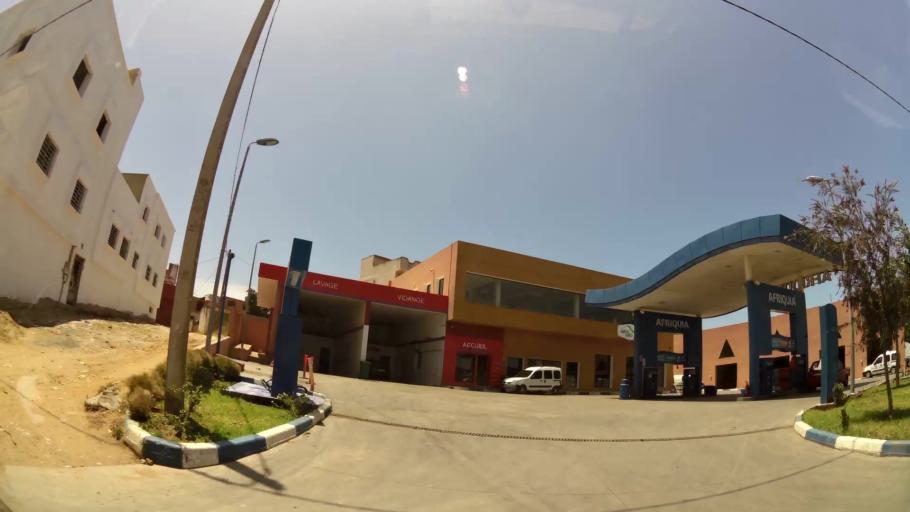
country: MA
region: Gharb-Chrarda-Beni Hssen
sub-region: Kenitra Province
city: Kenitra
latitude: 34.2657
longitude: -6.6440
